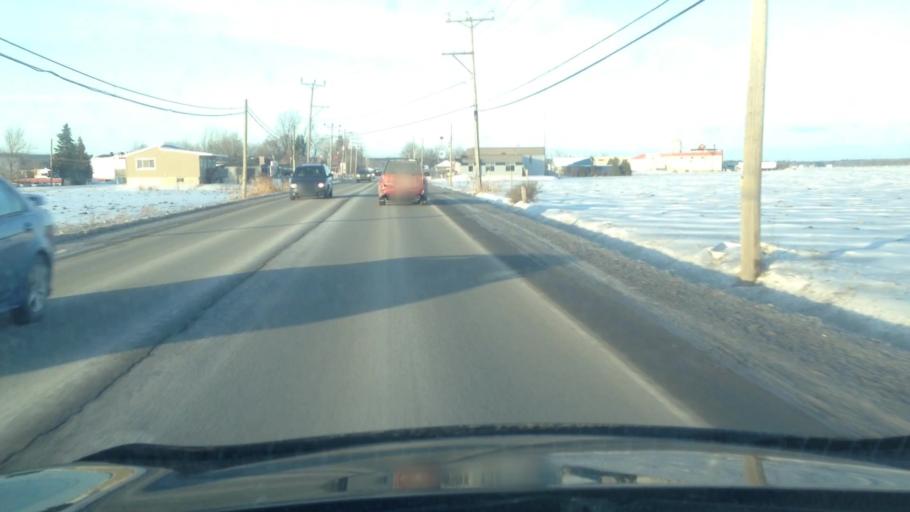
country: CA
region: Quebec
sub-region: Lanaudiere
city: Saint-Lin-Laurentides
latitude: 45.8830
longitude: -73.7577
